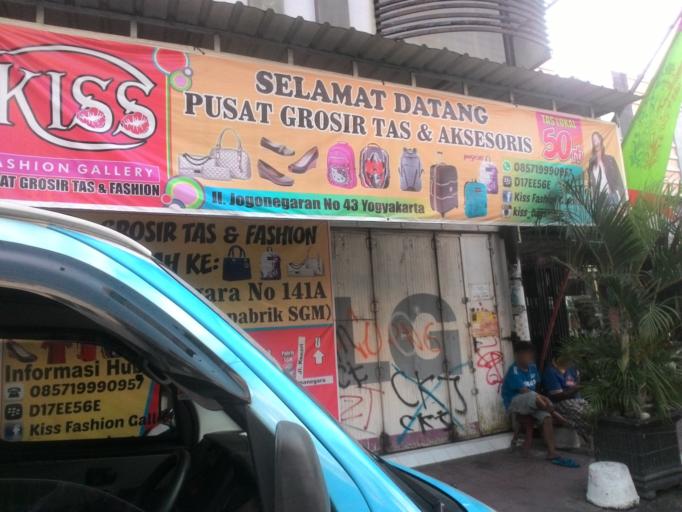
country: ID
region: Daerah Istimewa Yogyakarta
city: Yogyakarta
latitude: -7.7945
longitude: 110.3614
